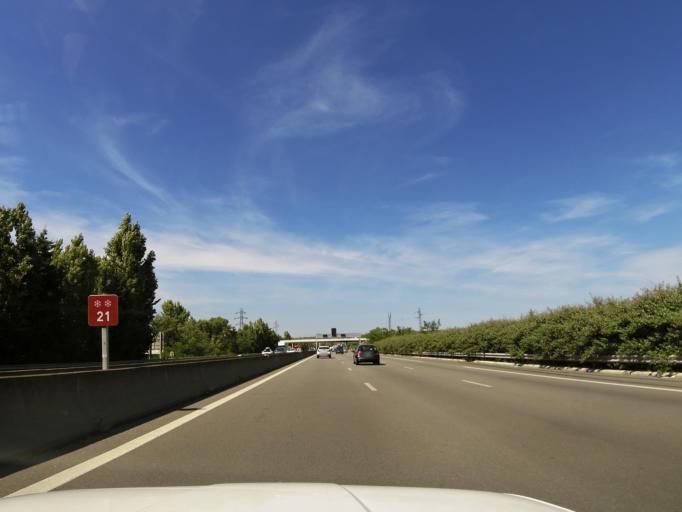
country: FR
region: Rhone-Alpes
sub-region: Departement de l'Isere
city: Salaise-sur-Sanne
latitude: 45.3466
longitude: 4.8071
